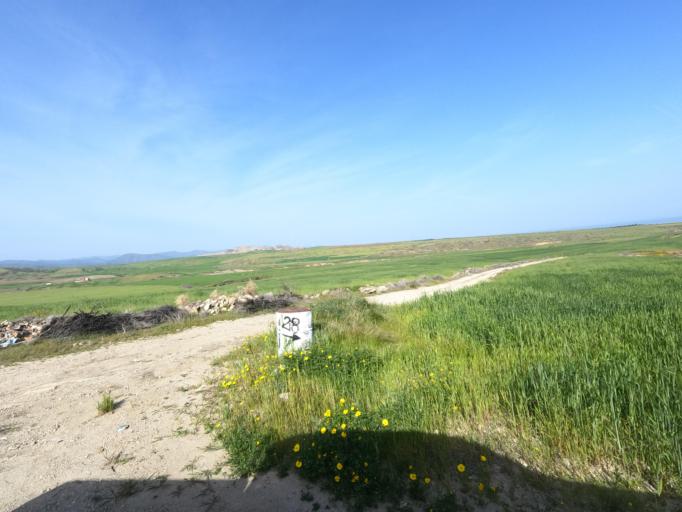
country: CY
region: Lefkosia
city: Astromeritis
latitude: 35.0964
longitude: 32.9505
